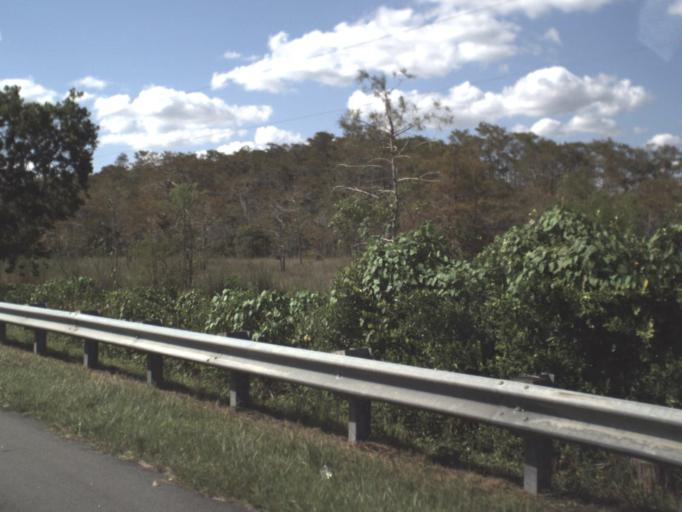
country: US
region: Florida
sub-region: Collier County
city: Lely Resort
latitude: 25.8644
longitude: -81.1071
